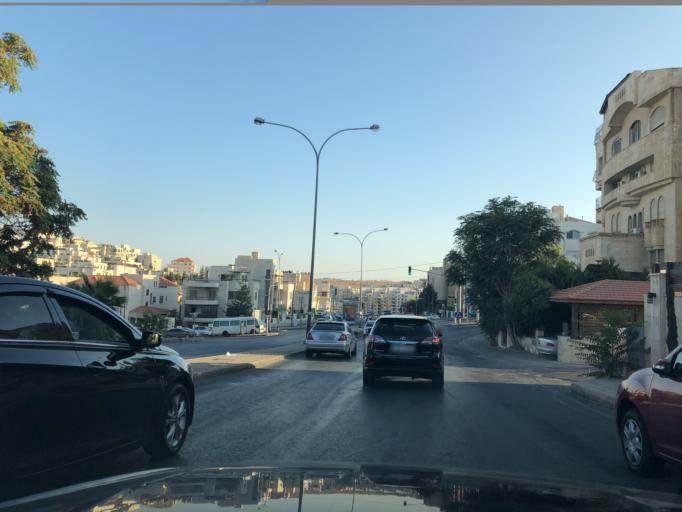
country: JO
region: Amman
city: Wadi as Sir
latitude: 31.9436
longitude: 35.8700
